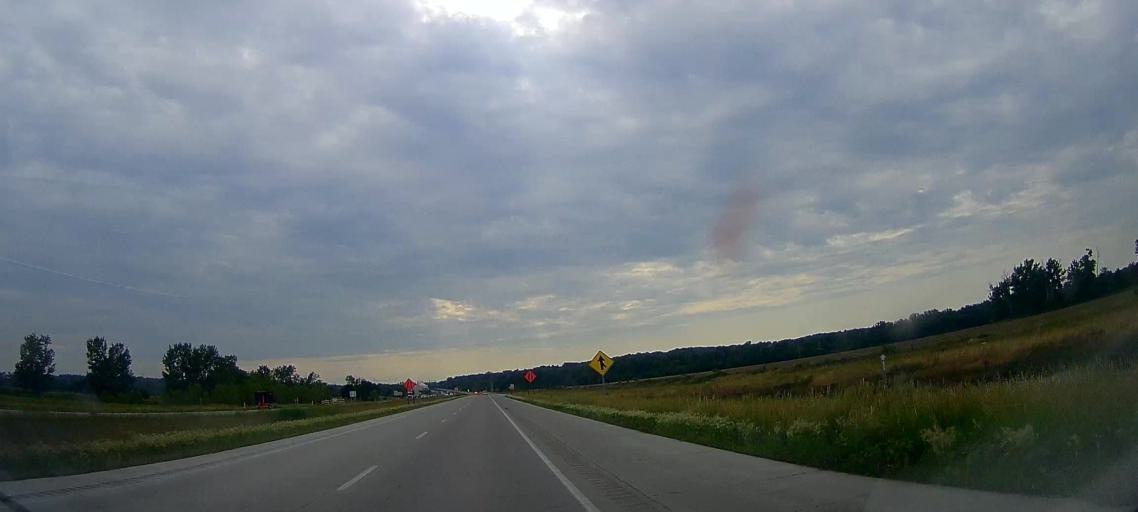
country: US
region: Iowa
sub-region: Pottawattamie County
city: Carter Lake
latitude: 41.3467
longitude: -95.9392
